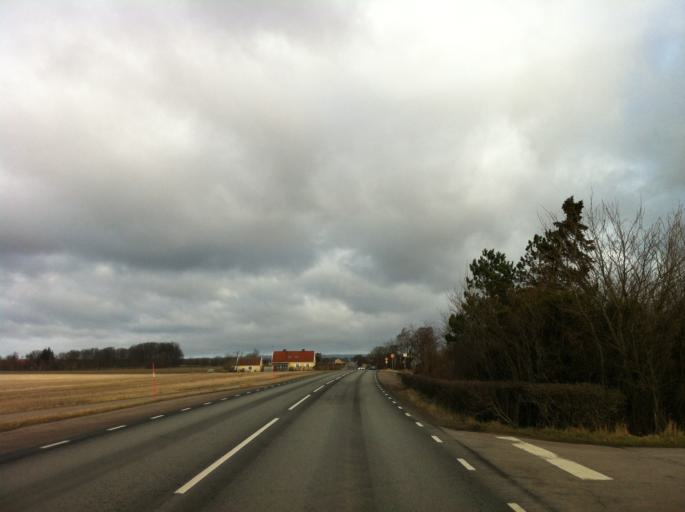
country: SE
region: Skane
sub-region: Angelholms Kommun
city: Strovelstorp
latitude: 56.1866
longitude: 12.8474
